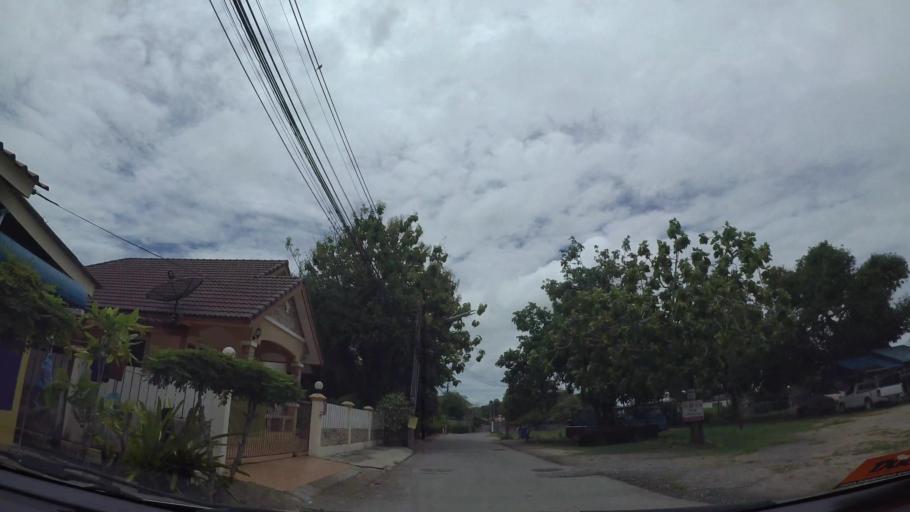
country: TH
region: Chon Buri
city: Sattahip
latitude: 12.7606
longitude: 100.8926
